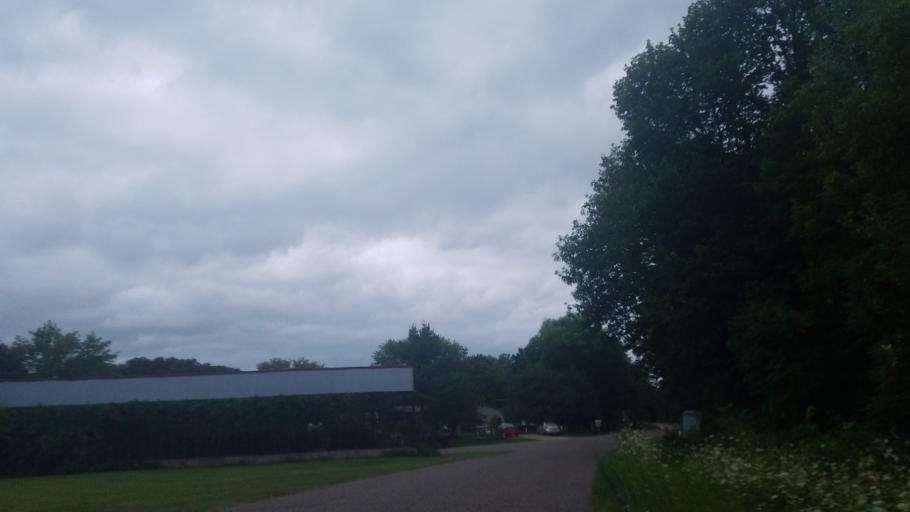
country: US
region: Wisconsin
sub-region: Dunn County
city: Menomonie
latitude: 44.8127
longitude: -91.9617
